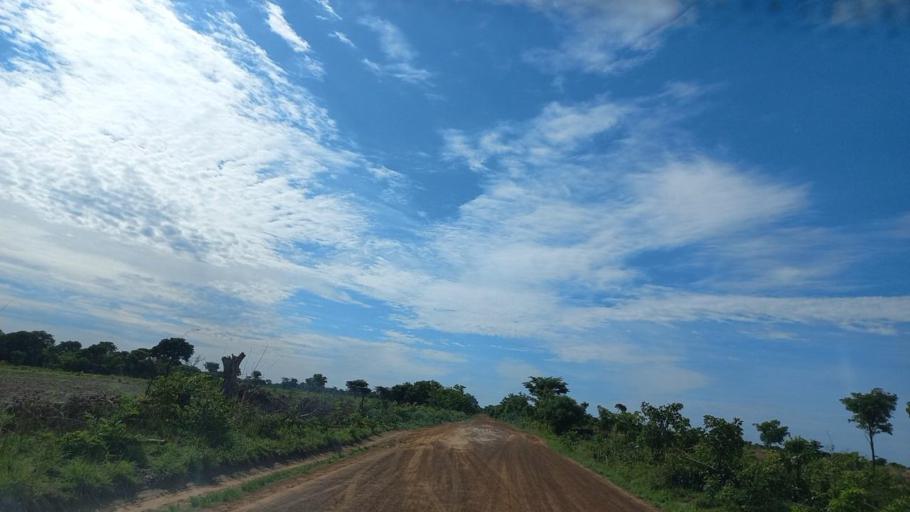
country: ZM
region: North-Western
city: Kabompo
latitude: -13.4334
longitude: 24.4196
